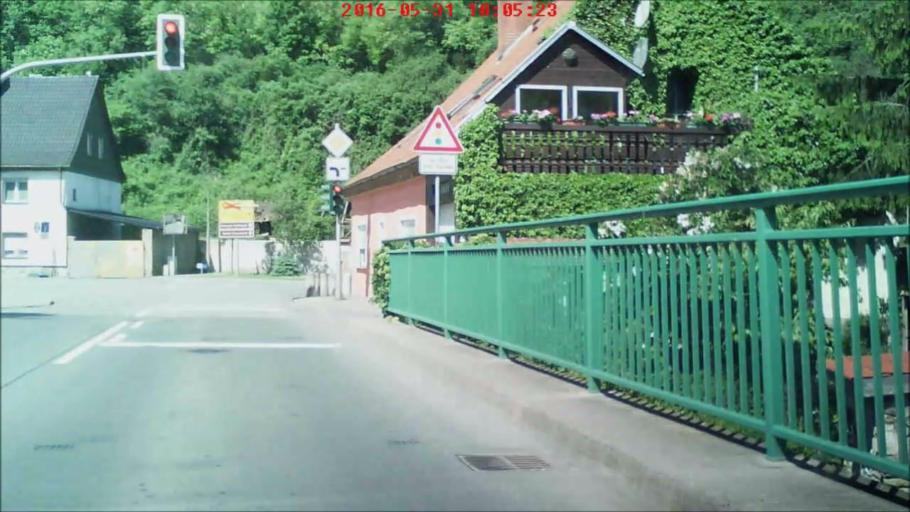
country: DE
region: Thuringia
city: Oldisleben
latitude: 51.2913
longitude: 11.1668
